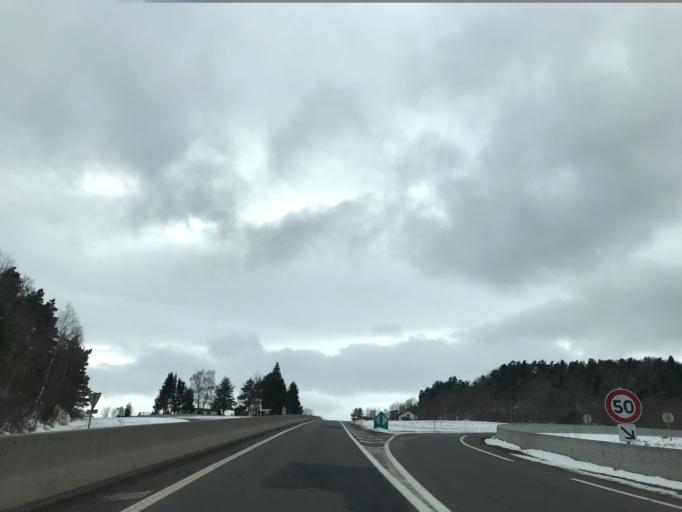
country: FR
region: Auvergne
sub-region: Departement du Puy-de-Dome
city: Saint-Genes-Champanelle
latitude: 45.6956
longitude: 2.9982
